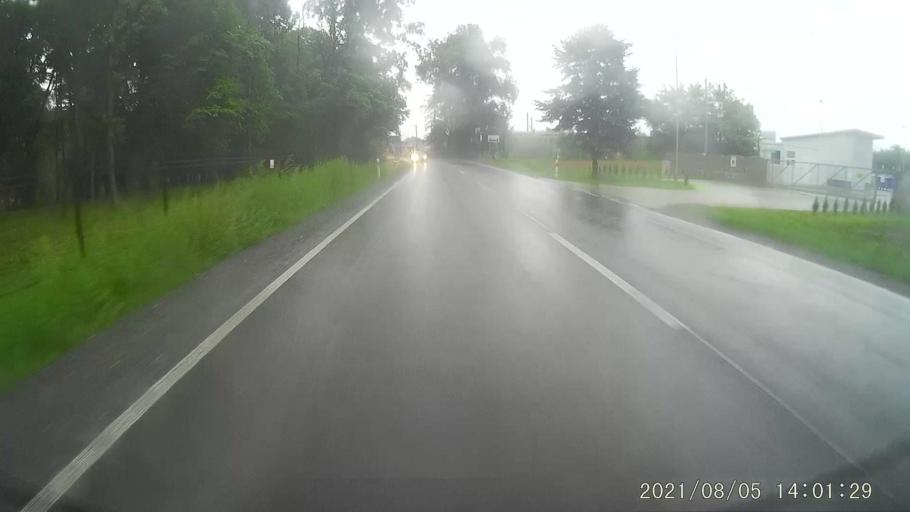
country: PL
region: Opole Voivodeship
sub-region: Powiat krapkowicki
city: Strzeleczki
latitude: 50.4482
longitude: 17.8917
